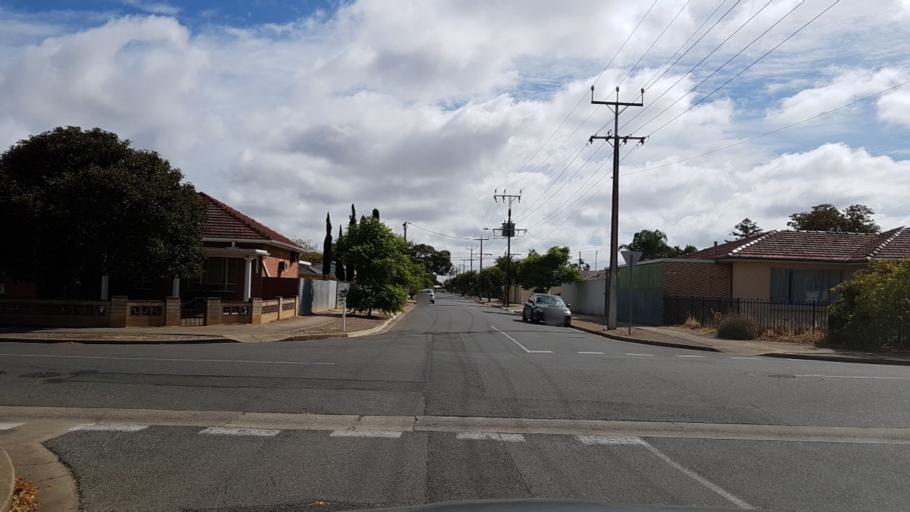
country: AU
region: South Australia
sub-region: Marion
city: Plympton Park
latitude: -34.9876
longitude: 138.5501
